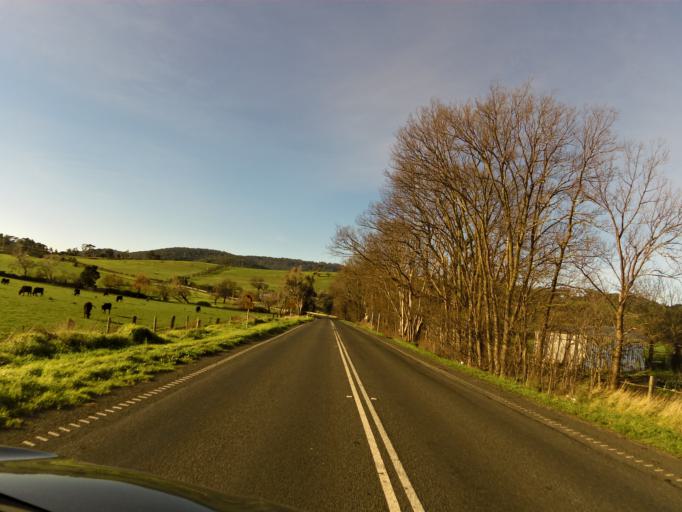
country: AU
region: Victoria
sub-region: Knox
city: Ferntree Gully
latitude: -37.9064
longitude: 145.2939
